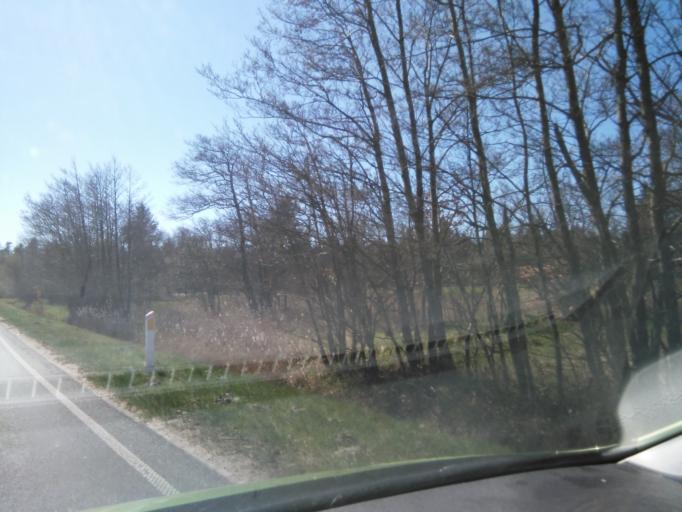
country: DK
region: South Denmark
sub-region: Varde Kommune
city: Oksbol
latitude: 55.5921
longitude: 8.2268
